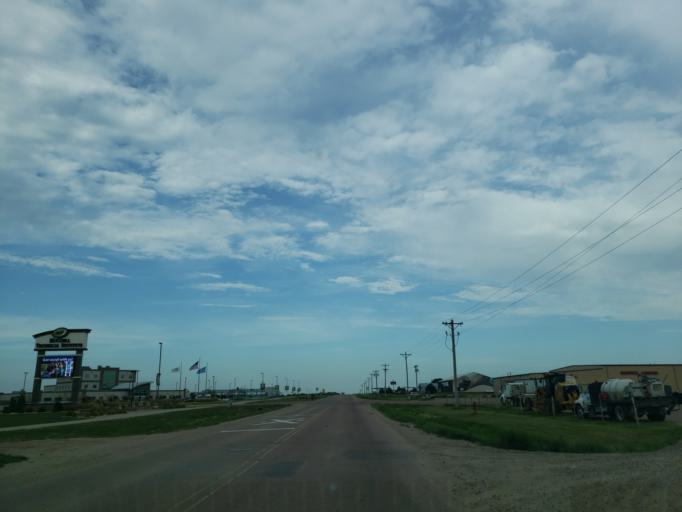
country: US
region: South Dakota
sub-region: Davison County
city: Mitchell
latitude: 43.6876
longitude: -98.0058
